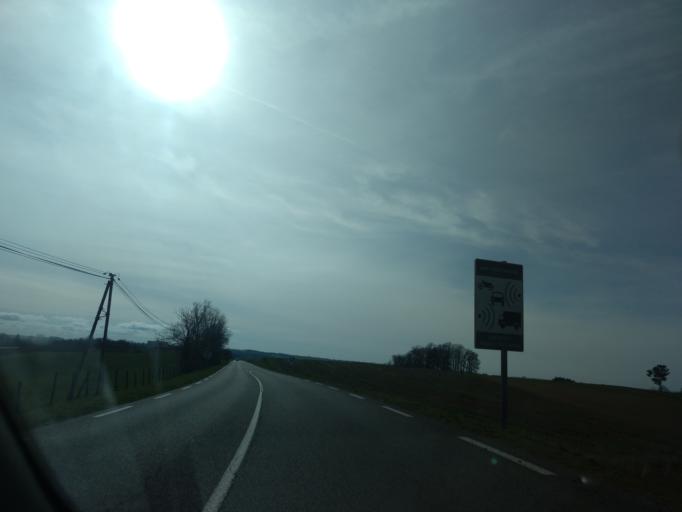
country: FR
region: Midi-Pyrenees
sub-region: Departement de l'Aveyron
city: Villeneuve
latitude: 44.4152
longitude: 2.0954
